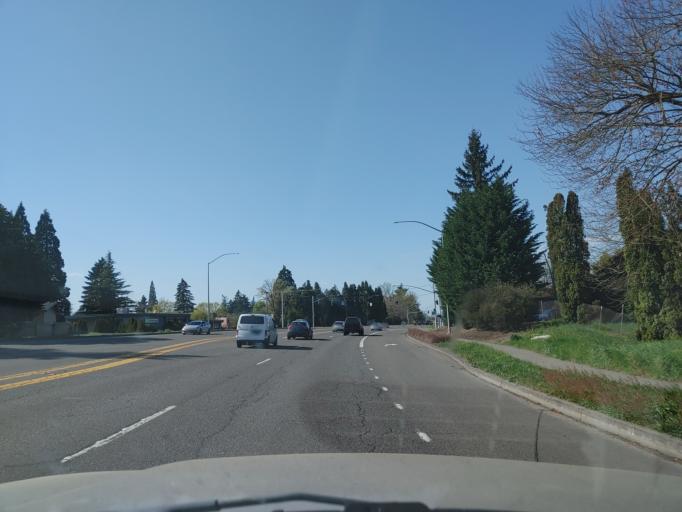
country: US
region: Oregon
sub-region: Clackamas County
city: Milwaukie
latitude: 45.4442
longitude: -122.6309
